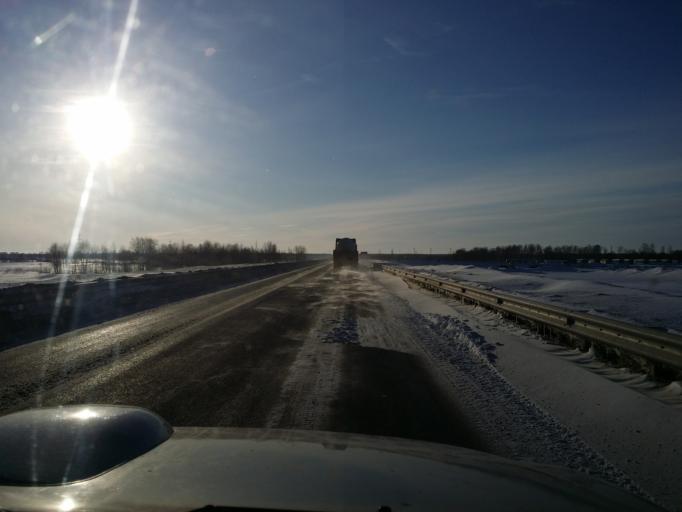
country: RU
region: Khanty-Mansiyskiy Avtonomnyy Okrug
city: Izluchinsk
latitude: 60.9366
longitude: 76.9420
